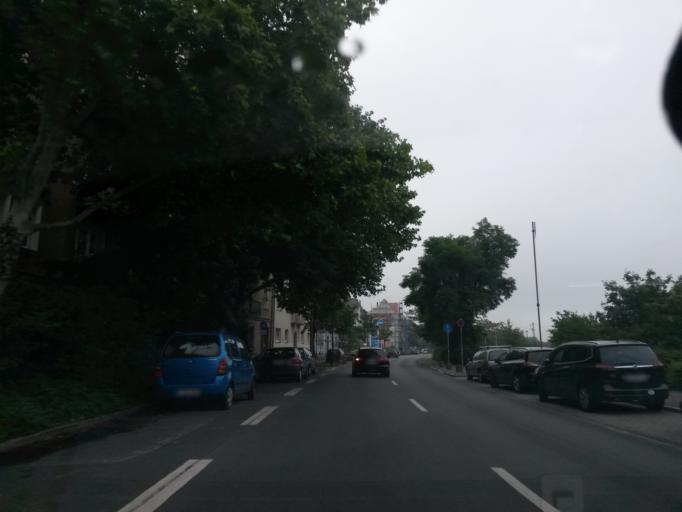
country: DE
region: Bavaria
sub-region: Regierungsbezirk Mittelfranken
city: Furth
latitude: 49.4679
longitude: 11.0036
